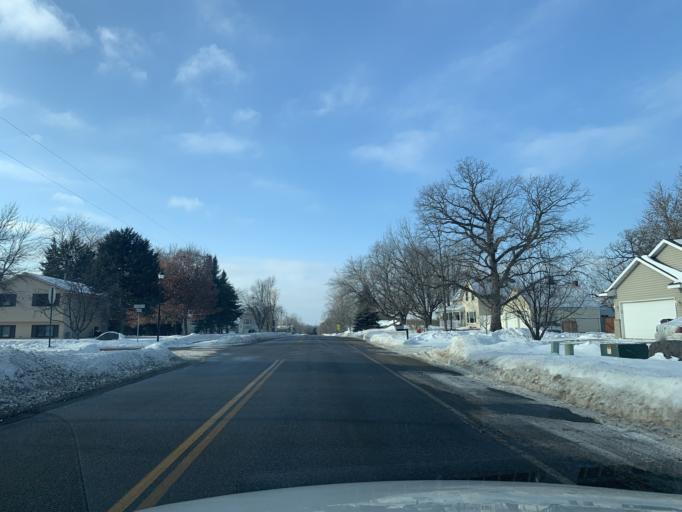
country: US
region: Minnesota
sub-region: Wright County
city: Buffalo
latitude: 45.1943
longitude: -93.8348
